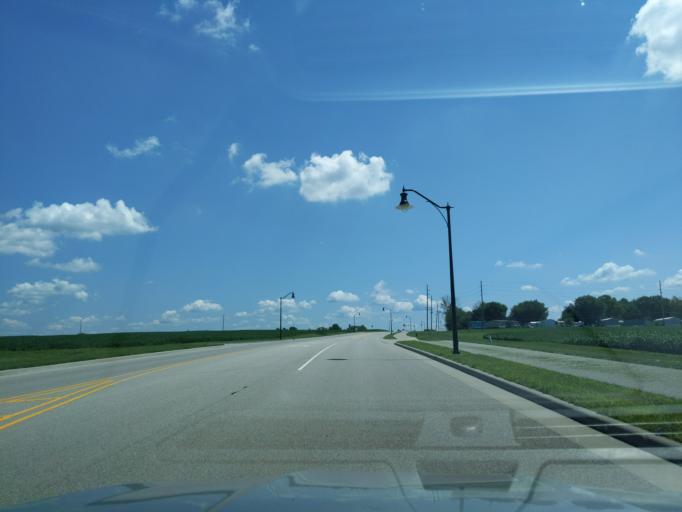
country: US
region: Indiana
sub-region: Decatur County
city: Greensburg
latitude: 39.3583
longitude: -85.5014
